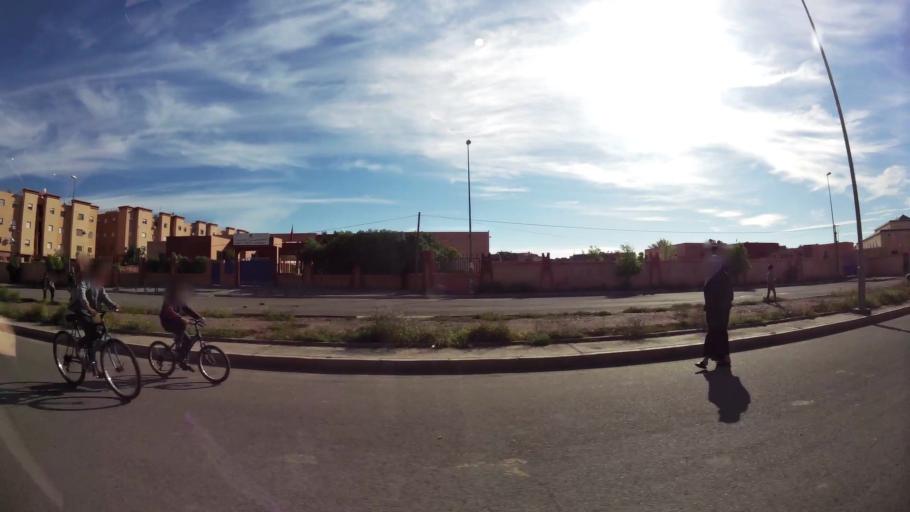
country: MA
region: Marrakech-Tensift-Al Haouz
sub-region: Marrakech
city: Marrakesh
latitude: 31.6878
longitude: -8.0709
